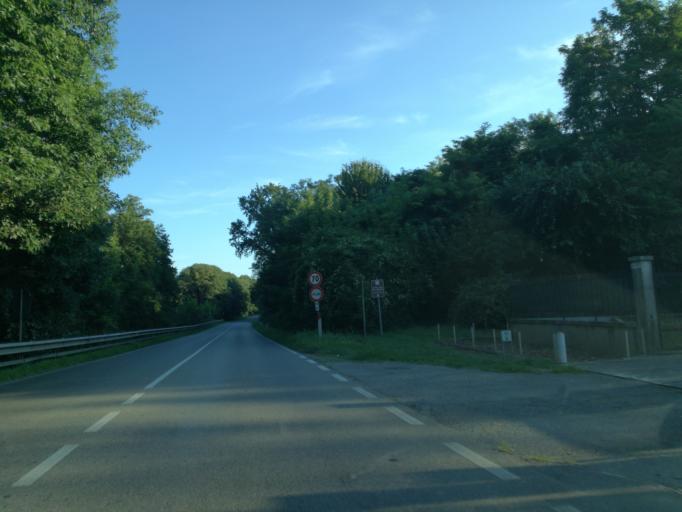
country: IT
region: Lombardy
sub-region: Provincia di Monza e Brianza
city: Aicurzio
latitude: 45.6325
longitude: 9.4134
